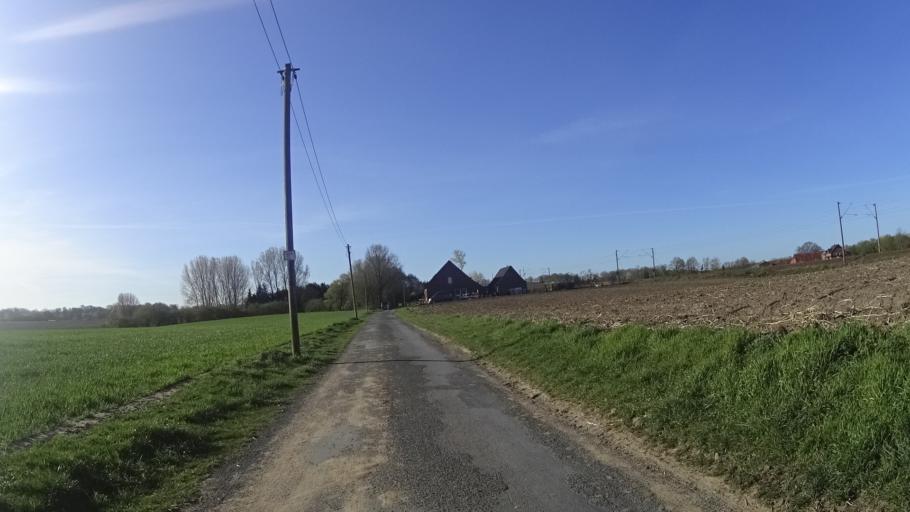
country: DE
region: North Rhine-Westphalia
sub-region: Regierungsbezirk Munster
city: Greven
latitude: 52.0805
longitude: 7.6042
